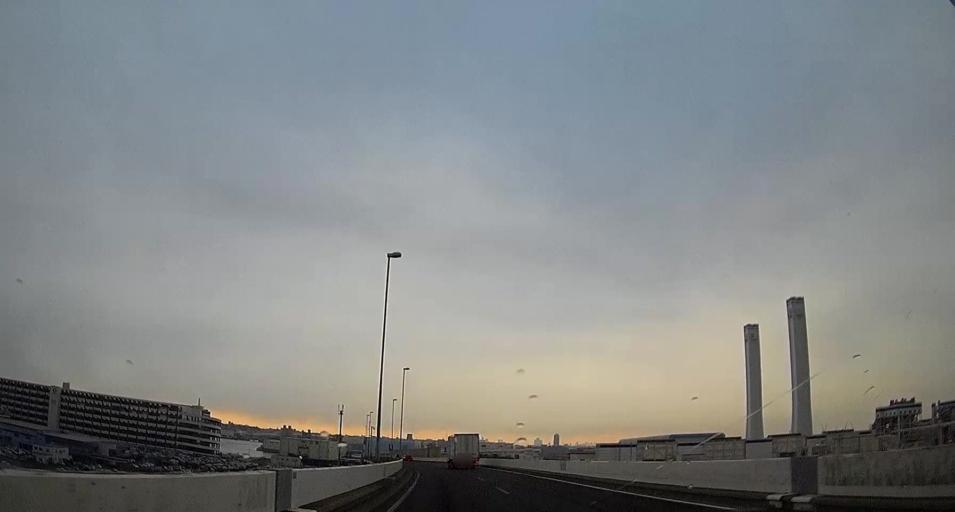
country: JP
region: Kanagawa
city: Yokohama
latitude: 35.4703
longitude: 139.6763
